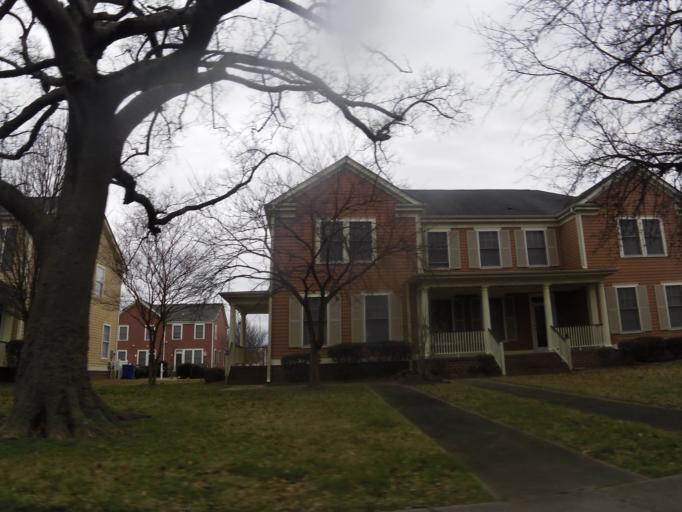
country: US
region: Virginia
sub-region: City of Portsmouth
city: Portsmouth
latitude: 36.8334
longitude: -76.3145
